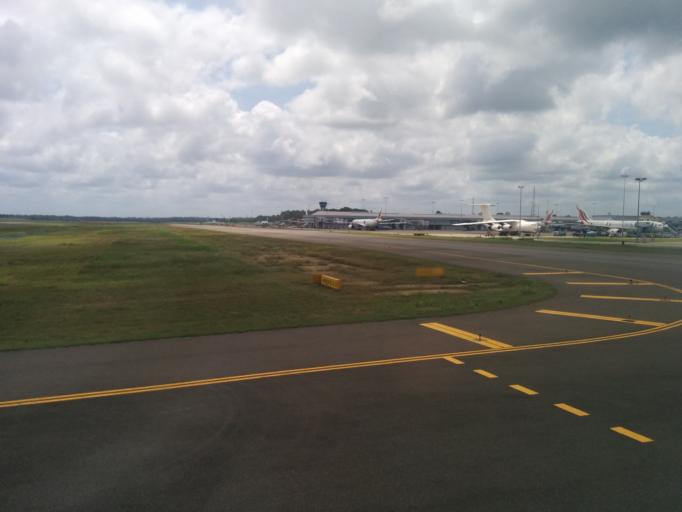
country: LK
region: Western
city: Katunayaka
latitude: 7.1745
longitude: 79.8802
